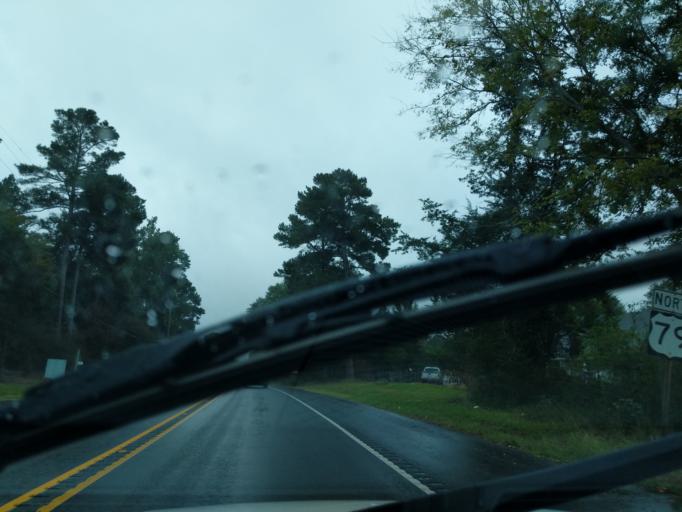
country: US
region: Louisiana
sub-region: Caddo Parish
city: Greenwood
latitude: 32.3747
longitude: -94.0337
